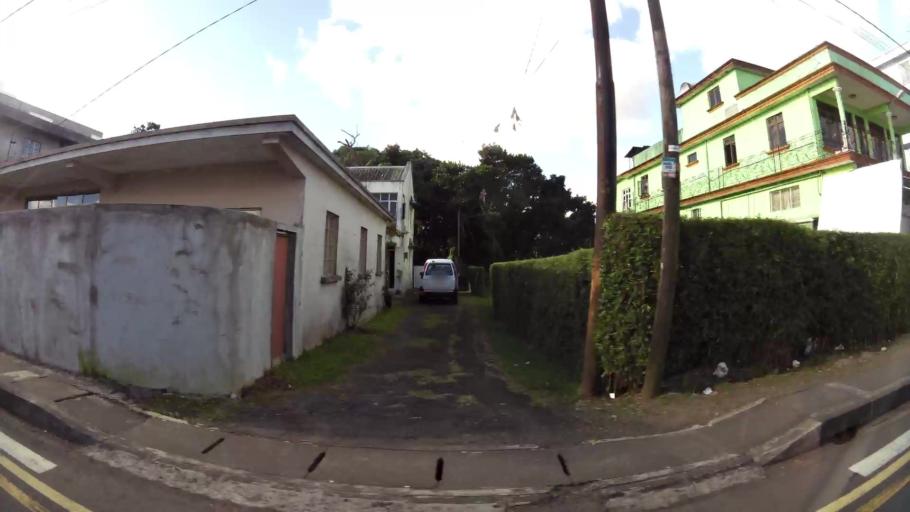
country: MU
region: Plaines Wilhems
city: Vacoas
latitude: -20.2854
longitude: 57.5069
